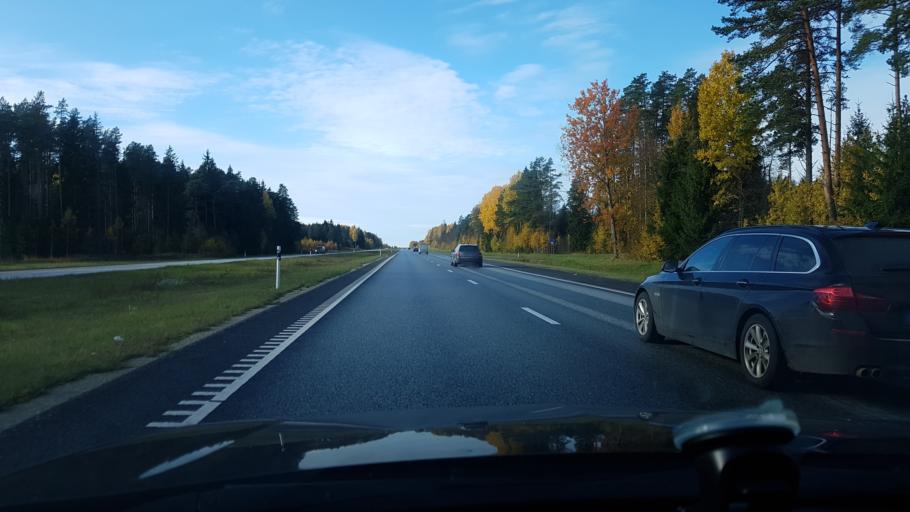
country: EE
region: Harju
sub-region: Raasiku vald
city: Raasiku
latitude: 59.4378
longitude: 25.2436
